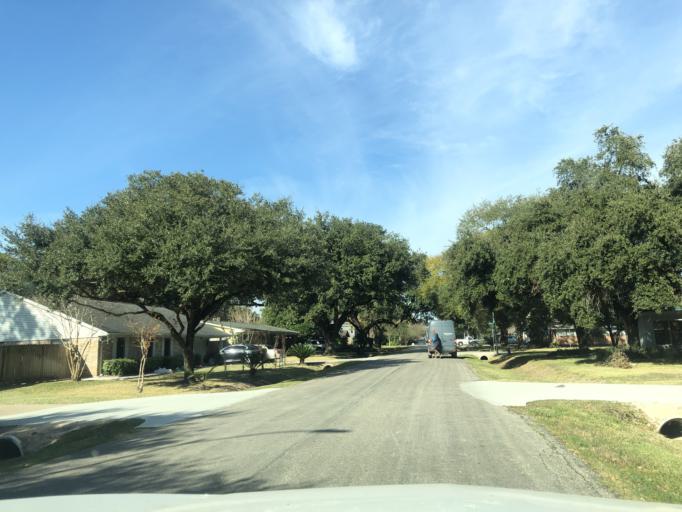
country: US
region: Texas
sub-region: Harris County
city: Bellaire
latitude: 29.6817
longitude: -95.5118
